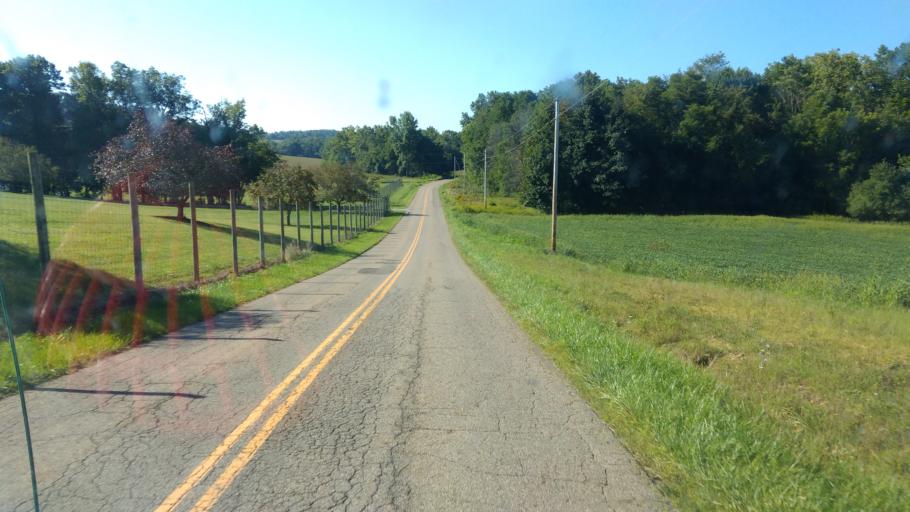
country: US
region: Ohio
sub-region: Knox County
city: Gambier
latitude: 40.4542
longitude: -82.3761
